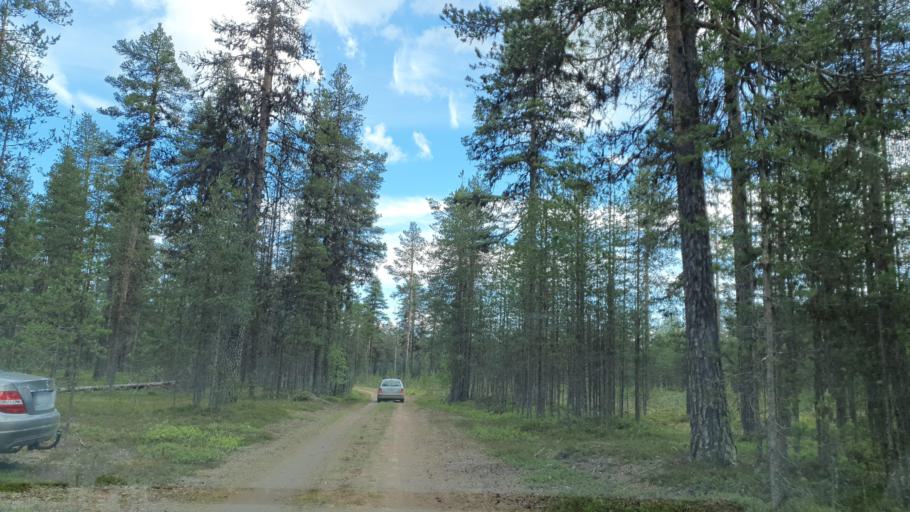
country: FI
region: Lapland
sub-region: Tunturi-Lappi
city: Kolari
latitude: 67.5392
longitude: 23.9135
